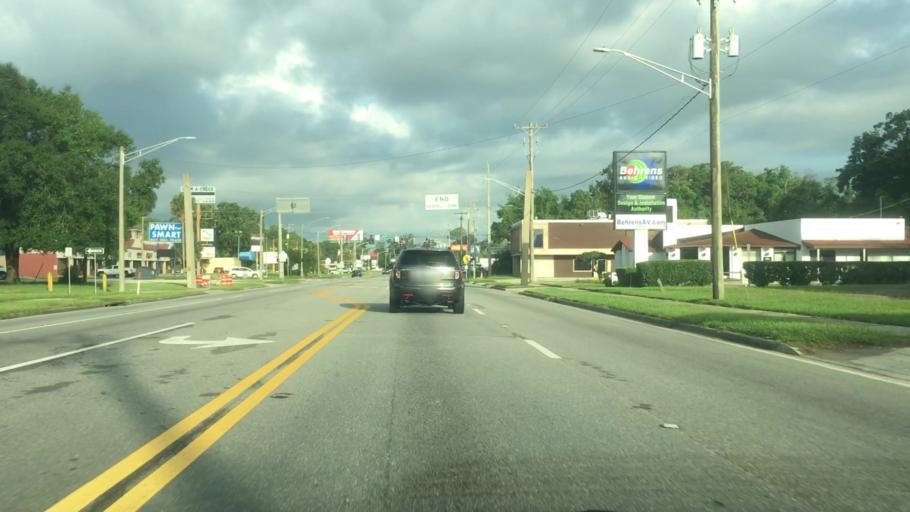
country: US
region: Florida
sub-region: Duval County
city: Jacksonville
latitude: 30.2906
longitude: -81.5909
